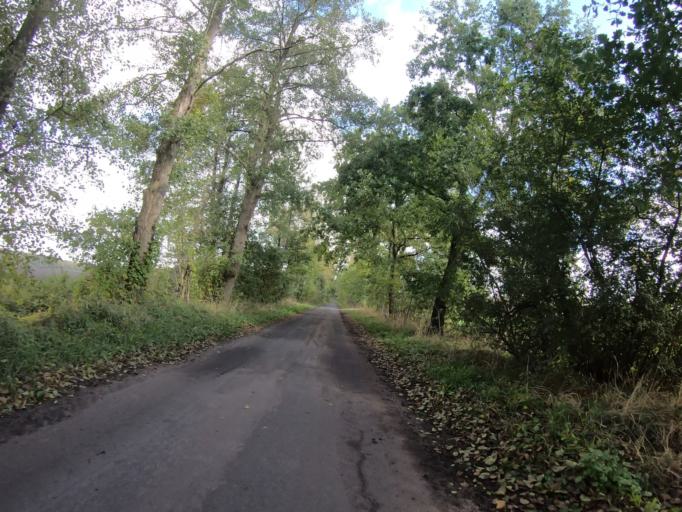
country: DE
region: Lower Saxony
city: Wagenhoff
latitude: 52.5408
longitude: 10.5474
